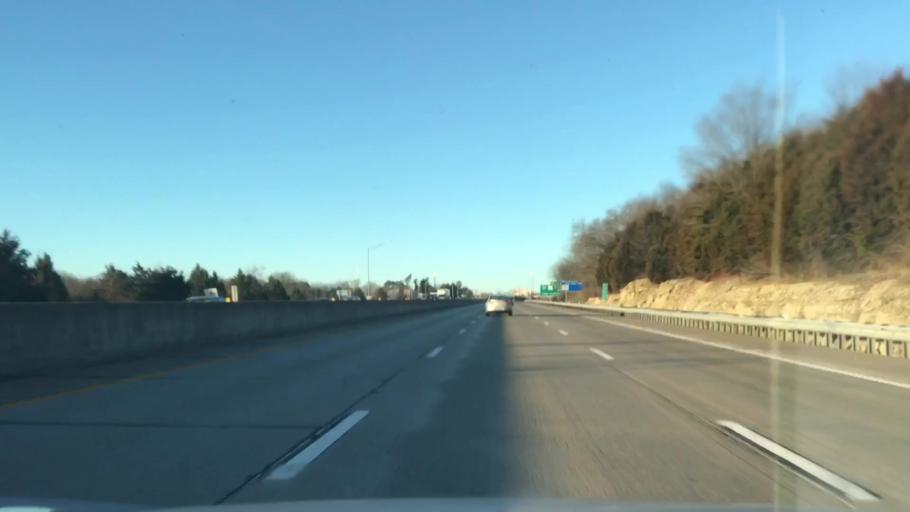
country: US
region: Missouri
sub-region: Franklin County
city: Gray Summit
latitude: 38.4859
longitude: -90.8134
